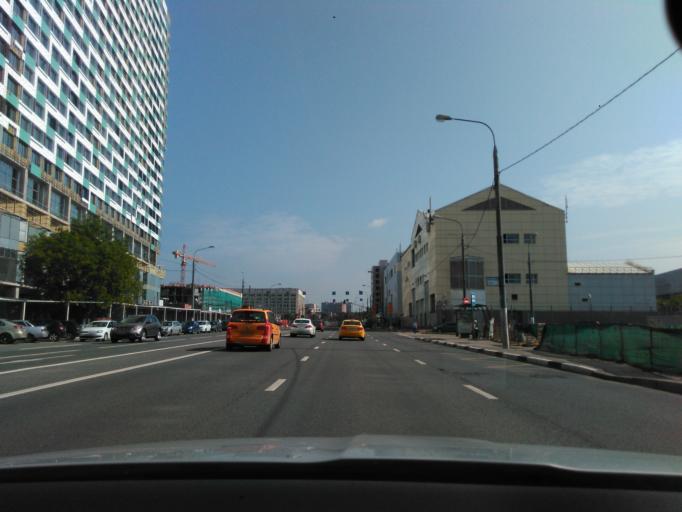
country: RU
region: Moscow
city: Sokol
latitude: 55.7856
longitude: 37.5423
